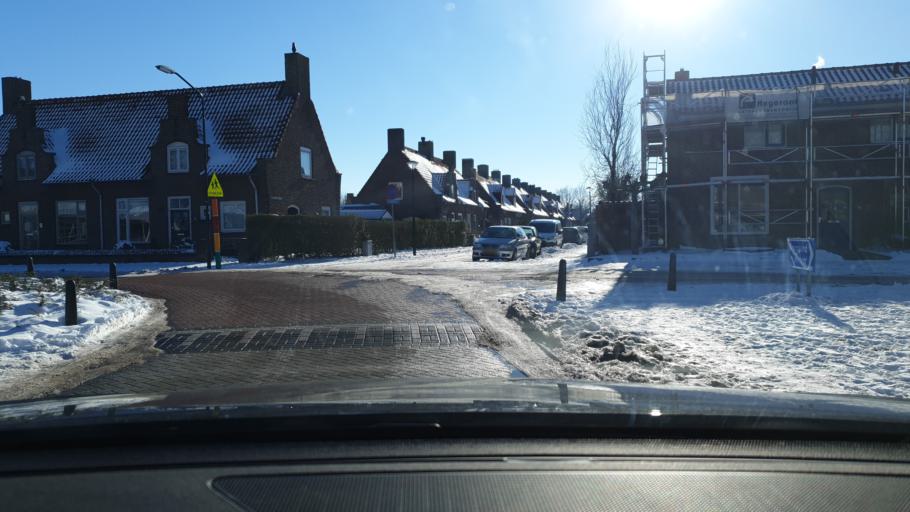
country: NL
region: North Brabant
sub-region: Gemeente Grave
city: Grave
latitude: 51.7576
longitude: 5.7304
